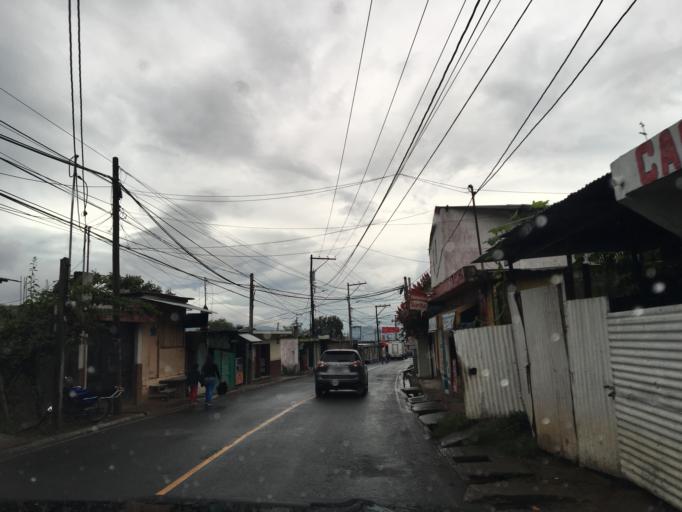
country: GT
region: Guatemala
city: Santa Catarina Pinula
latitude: 14.5474
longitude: -90.5101
